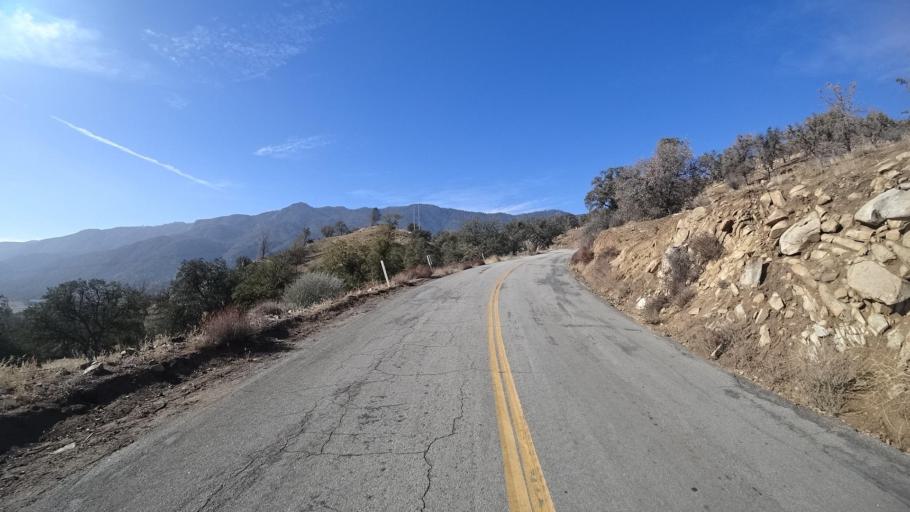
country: US
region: California
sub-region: Kern County
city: Bodfish
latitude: 35.4386
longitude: -118.5259
